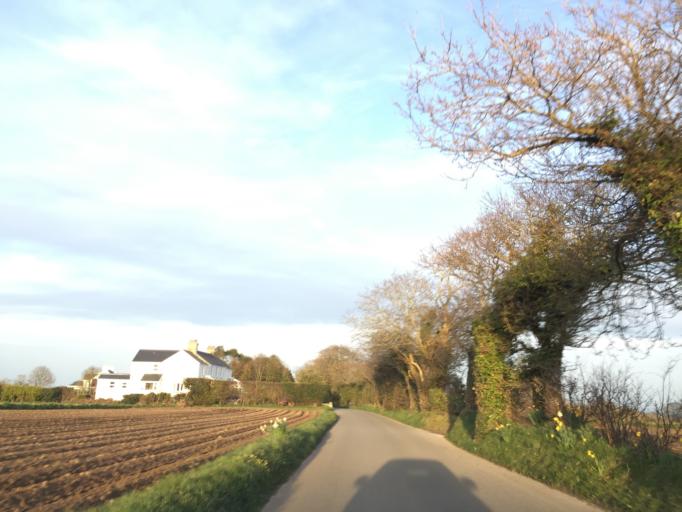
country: JE
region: St Helier
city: Saint Helier
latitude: 49.2282
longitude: -2.0543
